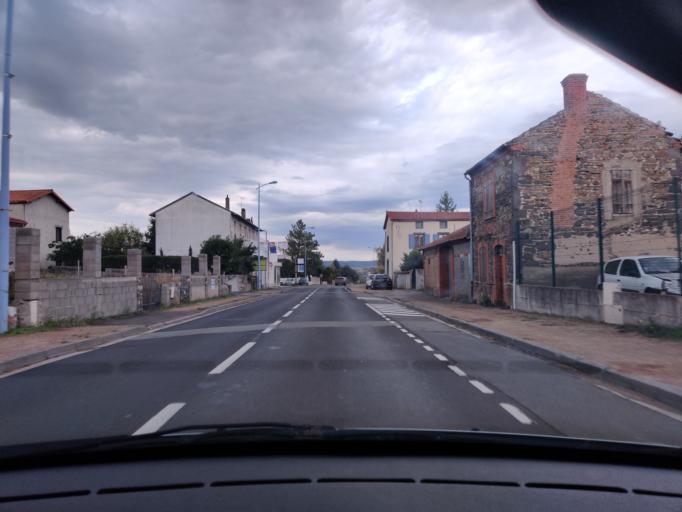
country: FR
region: Auvergne
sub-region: Departement du Puy-de-Dome
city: Combronde
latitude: 45.9857
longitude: 3.0872
